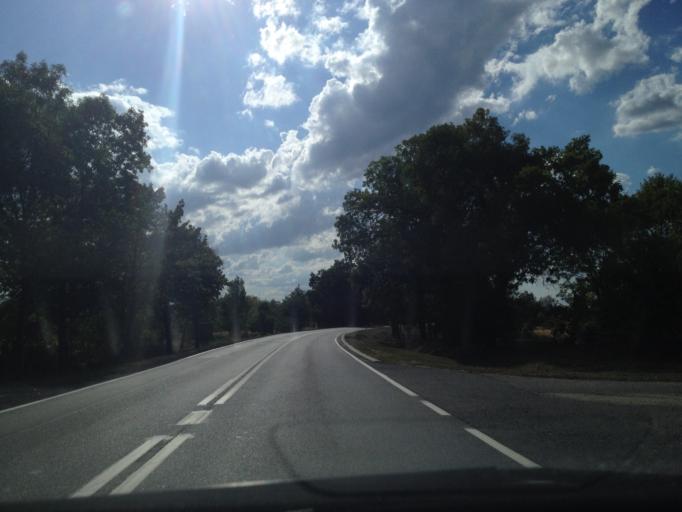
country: PL
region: Lubusz
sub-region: Powiat zarski
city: Sieniawa Zarska
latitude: 51.6305
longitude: 15.0909
